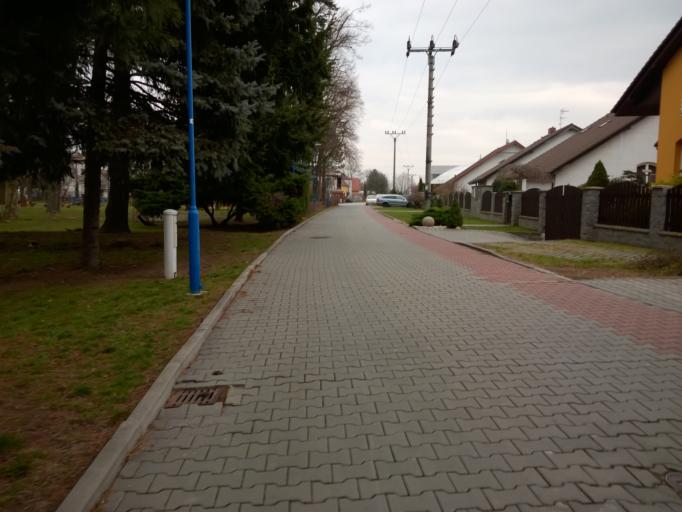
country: CZ
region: Pardubicky
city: Stare Hradiste
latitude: 50.0635
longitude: 15.7727
